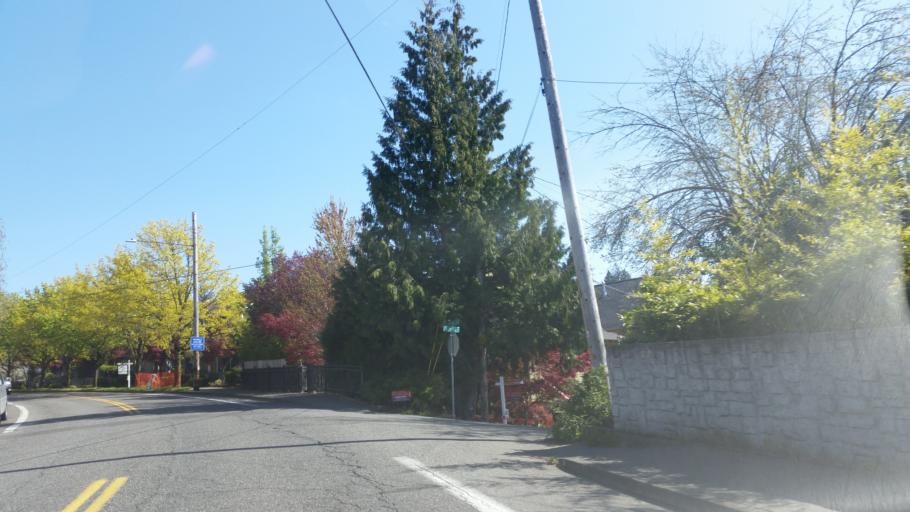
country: US
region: Oregon
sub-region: Washington County
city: Garden Home-Whitford
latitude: 45.4697
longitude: -122.7079
